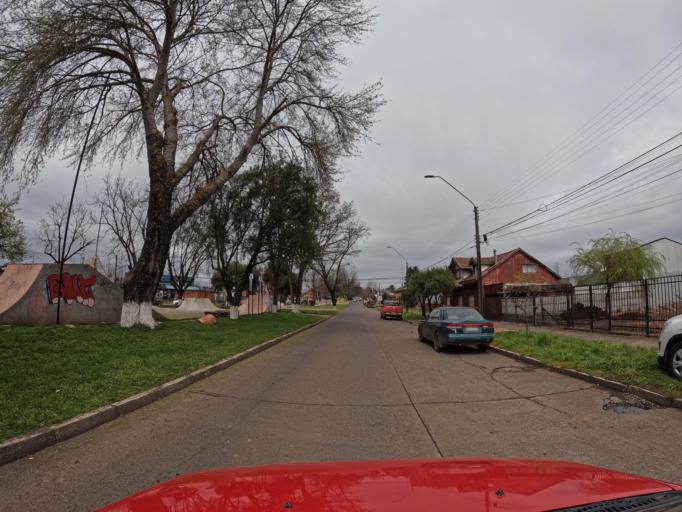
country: CL
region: Araucania
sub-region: Provincia de Malleco
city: Victoria
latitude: -38.2320
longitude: -72.3366
